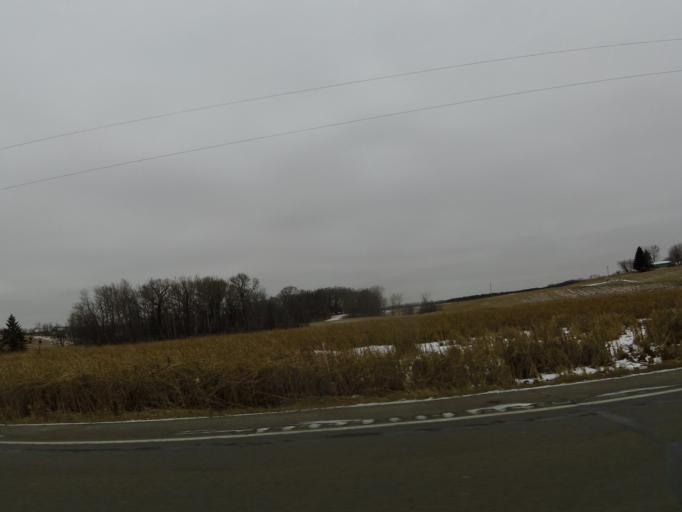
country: US
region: Minnesota
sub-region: Hennepin County
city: Independence
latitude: 45.0342
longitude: -93.7379
